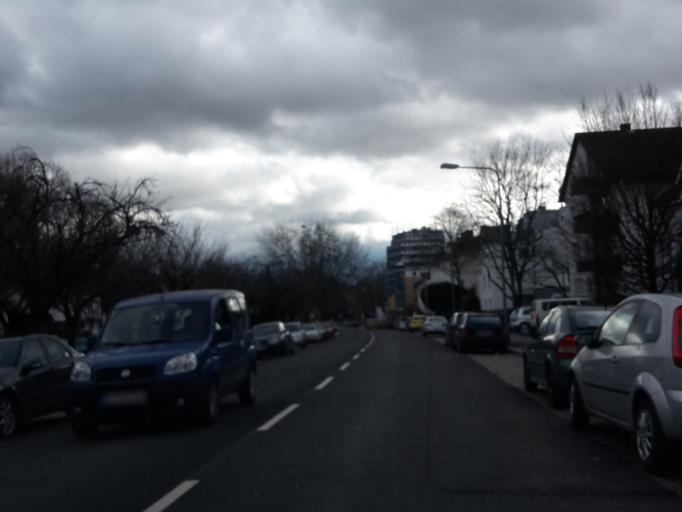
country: DE
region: Hesse
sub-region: Regierungsbezirk Darmstadt
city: Wiesbaden
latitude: 50.0886
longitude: 8.2208
